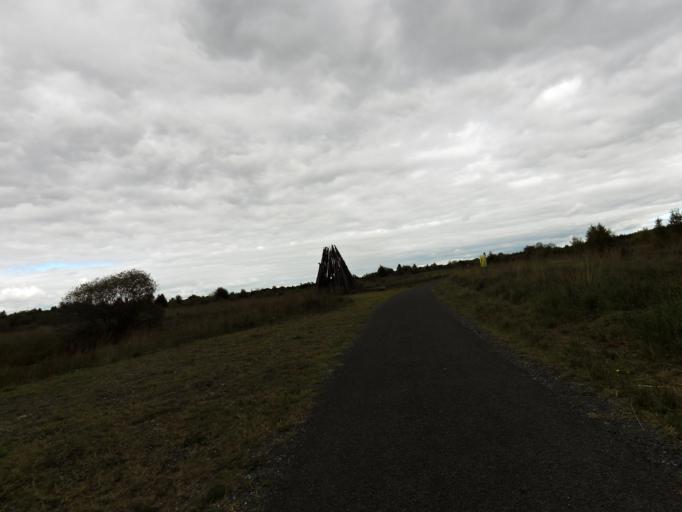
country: IE
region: Leinster
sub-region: Uibh Fhaili
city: Ferbane
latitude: 53.2216
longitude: -7.7514
